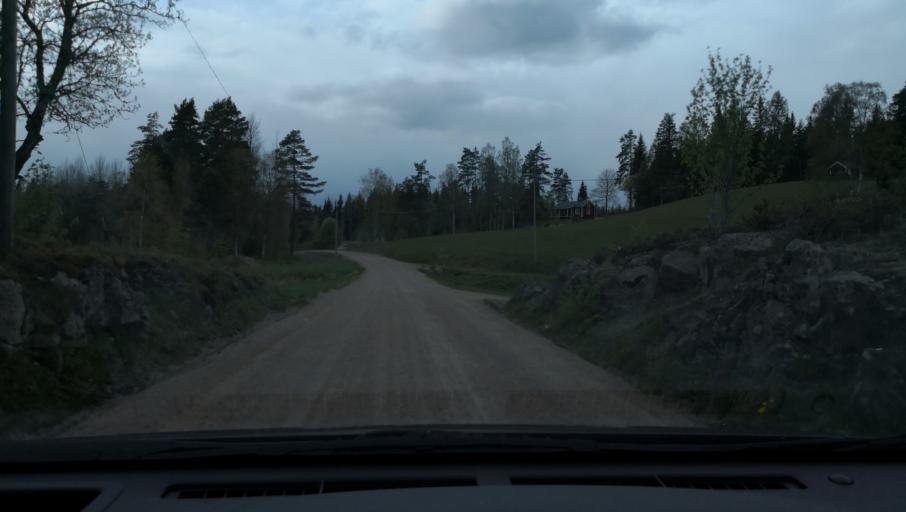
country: SE
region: Vaestmanland
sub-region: Fagersta Kommun
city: Fagersta
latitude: 60.1216
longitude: 15.7447
